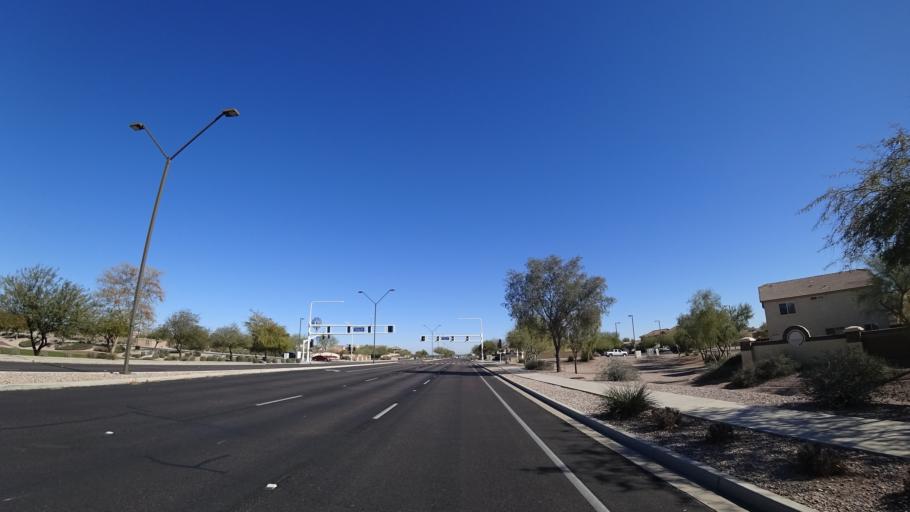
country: US
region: Arizona
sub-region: Maricopa County
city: Buckeye
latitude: 33.4356
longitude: -112.5271
